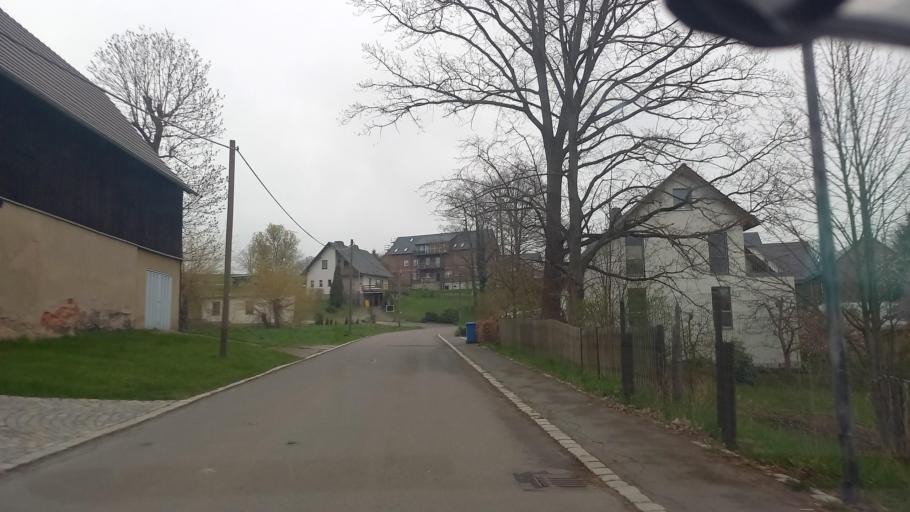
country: DE
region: Saxony
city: Reinsdorf
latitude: 50.6920
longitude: 12.5864
